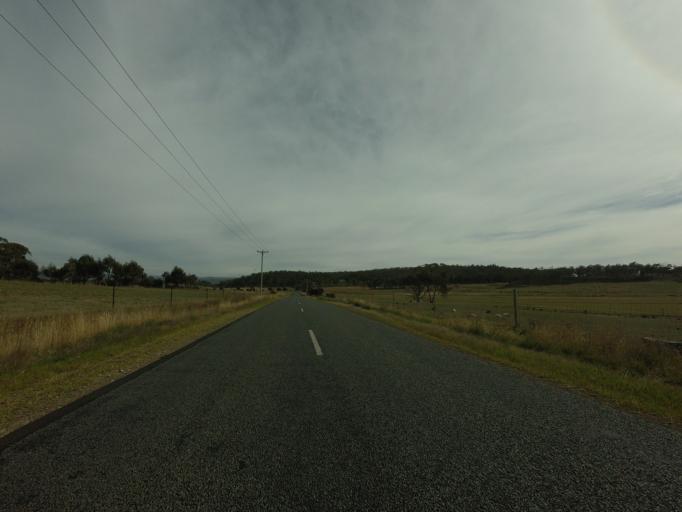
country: AU
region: Tasmania
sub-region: Brighton
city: Bridgewater
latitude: -42.3399
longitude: 147.4033
